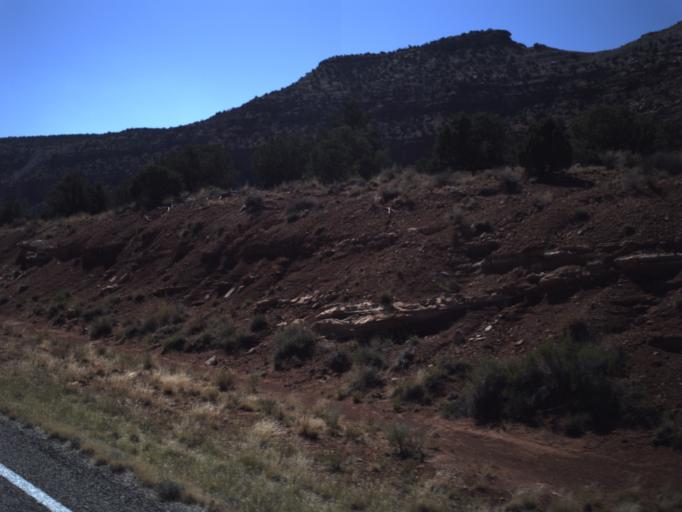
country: US
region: Utah
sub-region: San Juan County
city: Blanding
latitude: 37.6461
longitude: -110.1140
